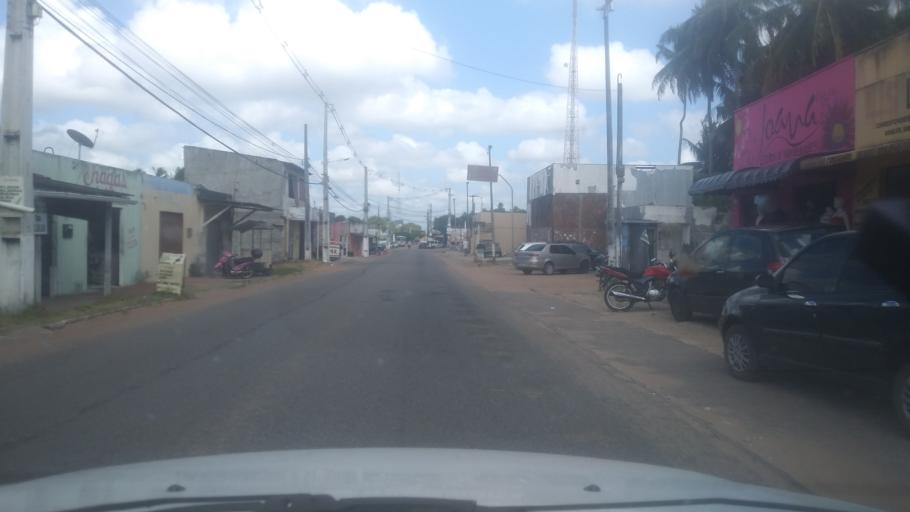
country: BR
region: Rio Grande do Norte
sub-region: Extremoz
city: Extremoz
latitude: -5.7059
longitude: -35.3020
